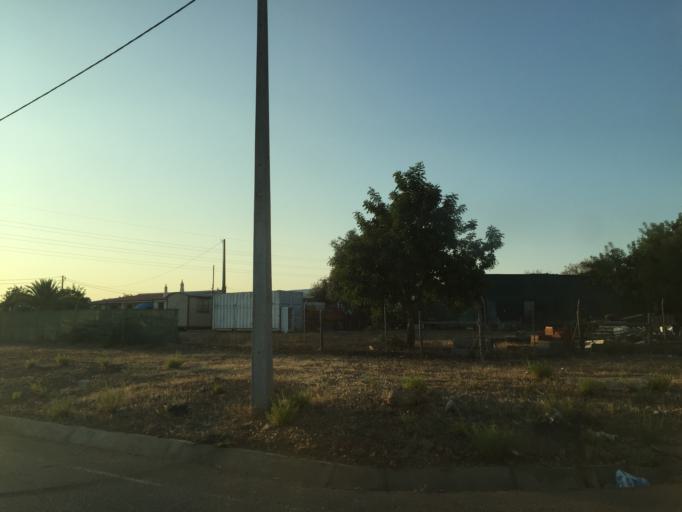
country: PT
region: Faro
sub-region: Olhao
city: Olhao
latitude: 37.0836
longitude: -7.8533
